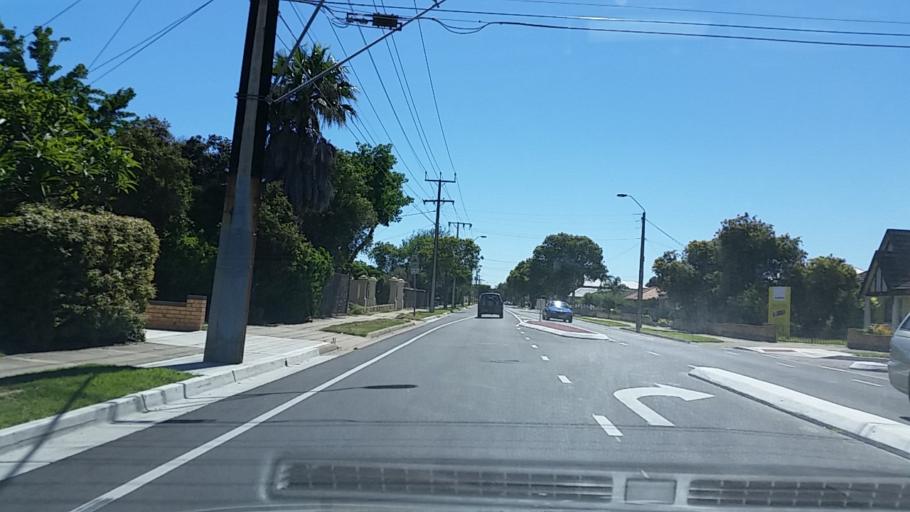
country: AU
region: South Australia
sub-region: Charles Sturt
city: Findon
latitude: -34.9118
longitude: 138.5445
